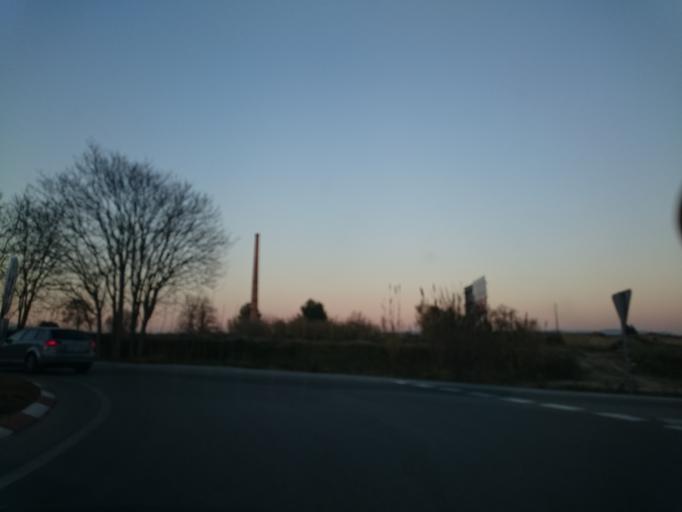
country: ES
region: Catalonia
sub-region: Provincia de Barcelona
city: Vilafranca del Penedes
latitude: 41.3538
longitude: 1.7066
